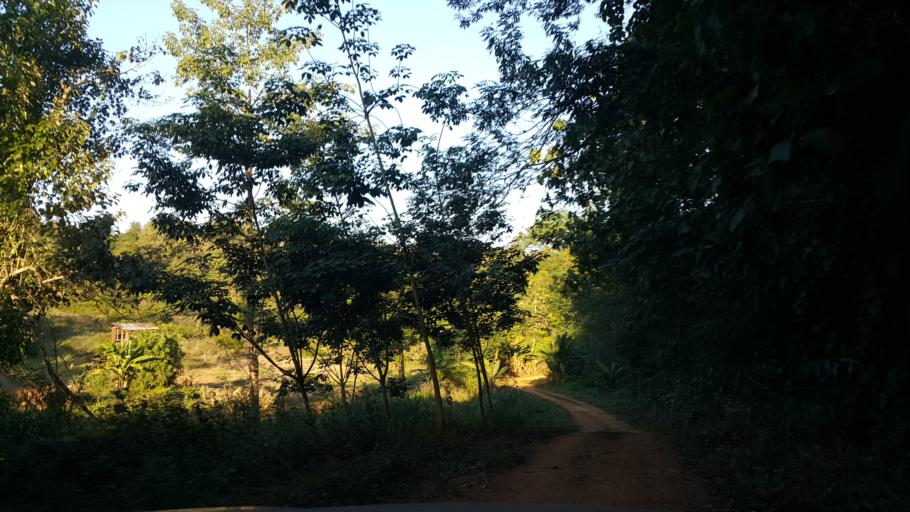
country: TH
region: Sukhothai
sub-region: Amphoe Si Satchanalai
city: Si Satchanalai
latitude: 17.5838
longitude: 99.6029
